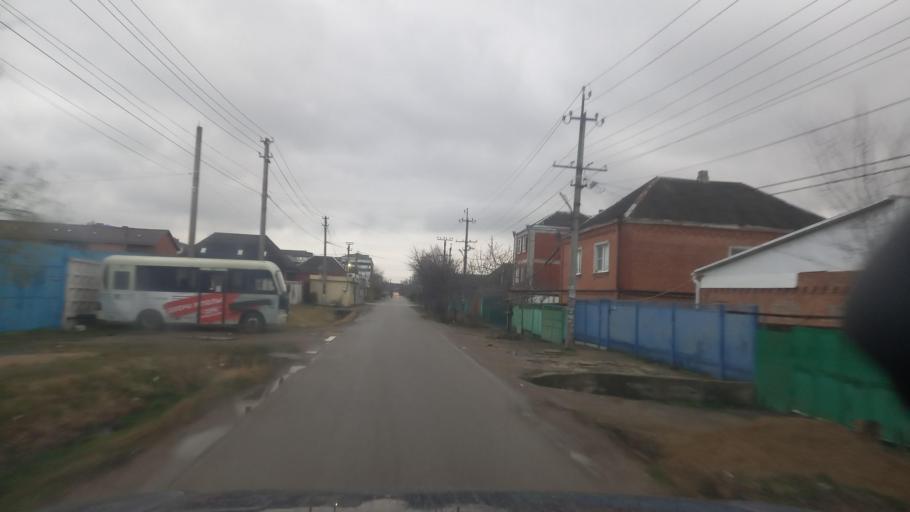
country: RU
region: Adygeya
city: Yablonovskiy
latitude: 44.9834
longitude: 38.9326
